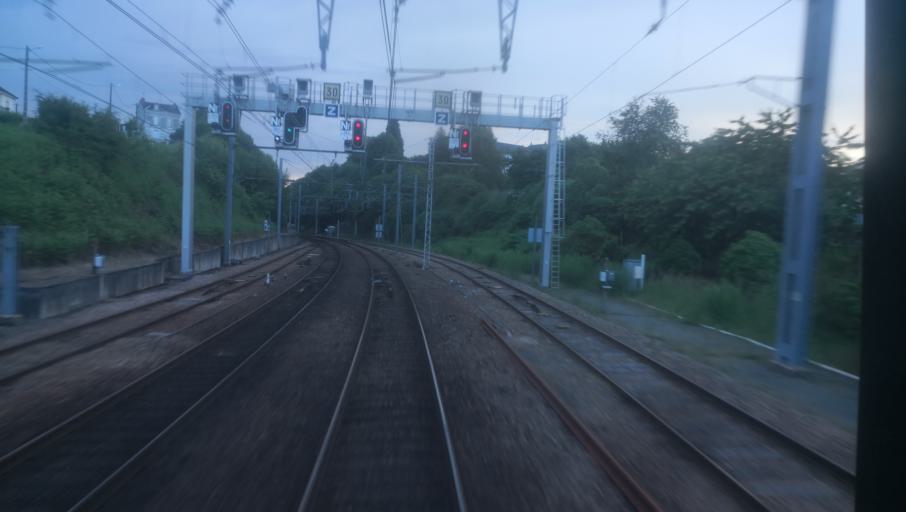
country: FR
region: Limousin
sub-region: Departement de la Haute-Vienne
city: Ambazac
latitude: 46.0510
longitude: 1.4714
